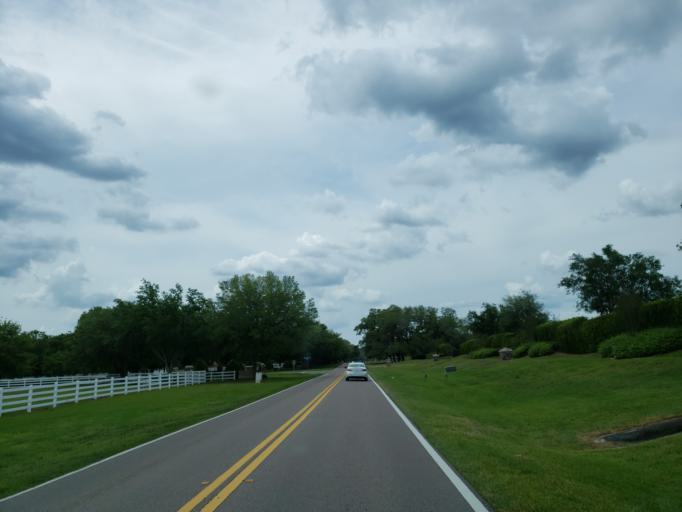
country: US
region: Florida
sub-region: Hillsborough County
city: Keystone
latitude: 28.1231
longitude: -82.6121
